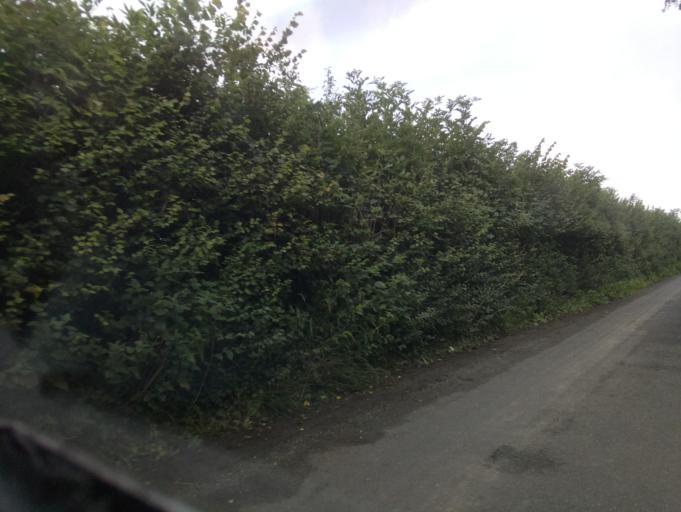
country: GB
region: England
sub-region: Somerset
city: Evercreech
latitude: 51.1457
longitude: -2.4900
